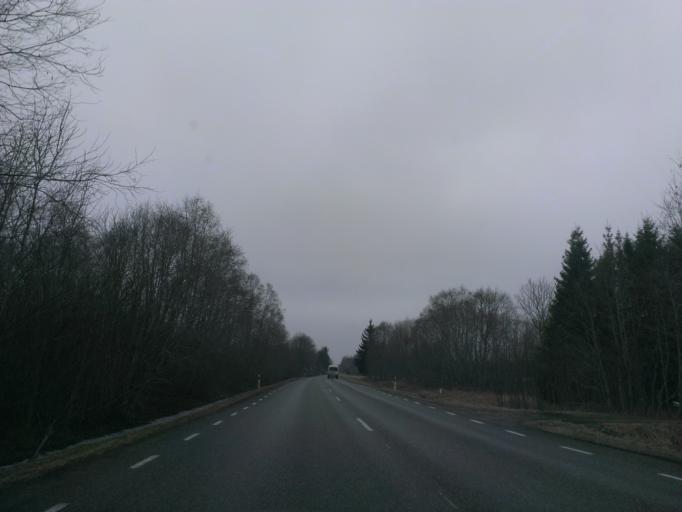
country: EE
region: Paernumaa
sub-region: Audru vald
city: Audru
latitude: 58.4842
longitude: 24.1544
